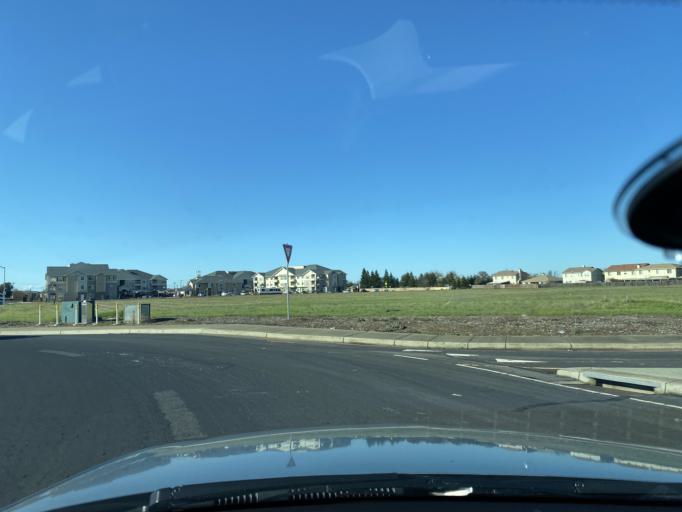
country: US
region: California
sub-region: Sacramento County
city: Laguna
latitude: 38.4401
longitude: -121.3972
